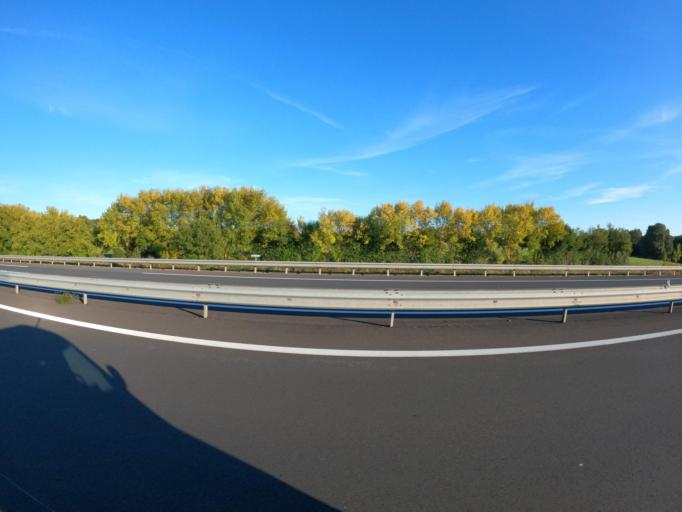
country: FR
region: Pays de la Loire
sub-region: Departement de la Vendee
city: Saint-Fulgent
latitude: 46.8398
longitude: -1.1537
